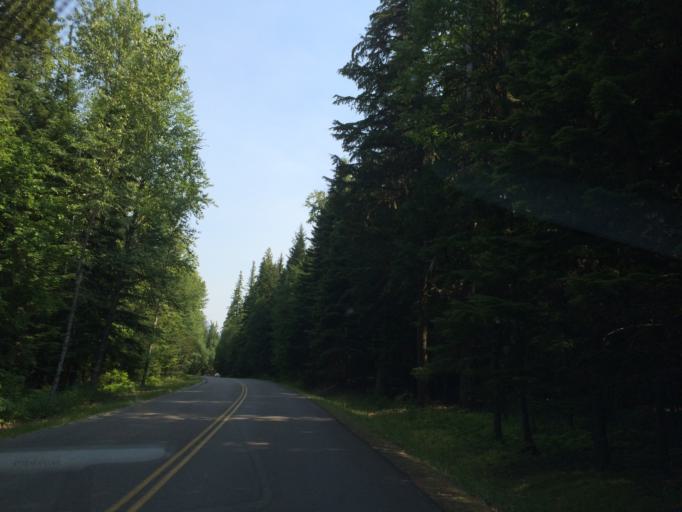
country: US
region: Montana
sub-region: Flathead County
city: Columbia Falls
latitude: 48.6201
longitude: -113.8725
